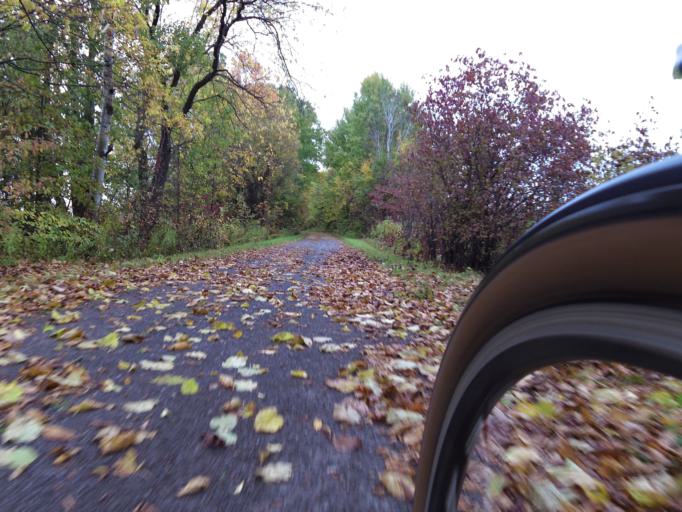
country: CA
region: Quebec
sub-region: Outaouais
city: Shawville
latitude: 45.7015
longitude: -76.5816
